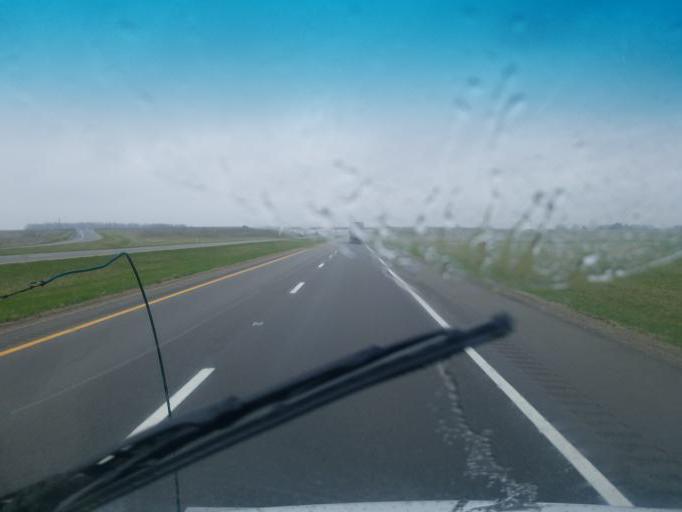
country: US
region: Ohio
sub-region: Wyandot County
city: Upper Sandusky
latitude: 40.8357
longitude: -83.3339
